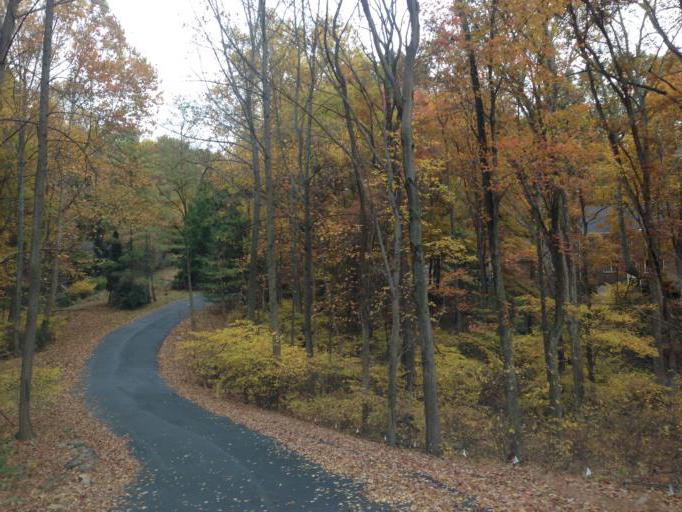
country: US
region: Maryland
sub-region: Howard County
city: Highland
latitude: 39.2710
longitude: -76.9447
